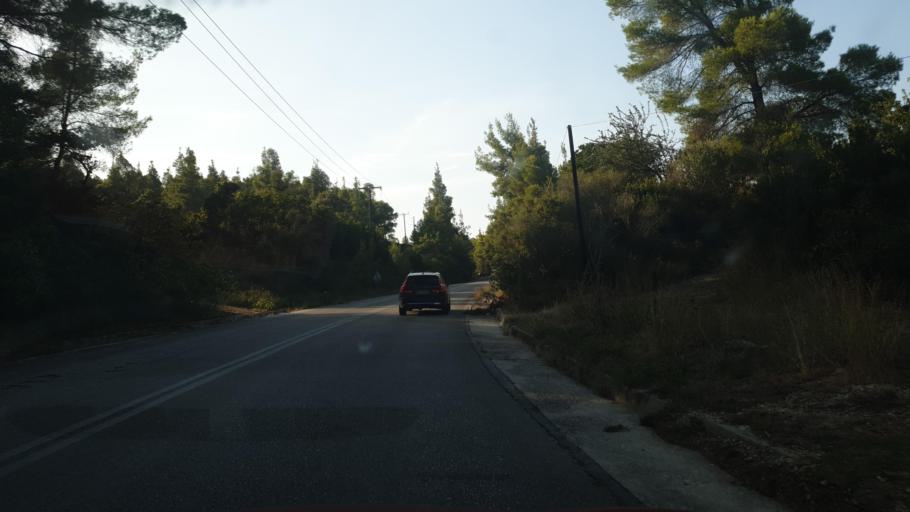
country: GR
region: Central Macedonia
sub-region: Nomos Chalkidikis
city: Neos Marmaras
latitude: 40.1777
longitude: 23.8288
